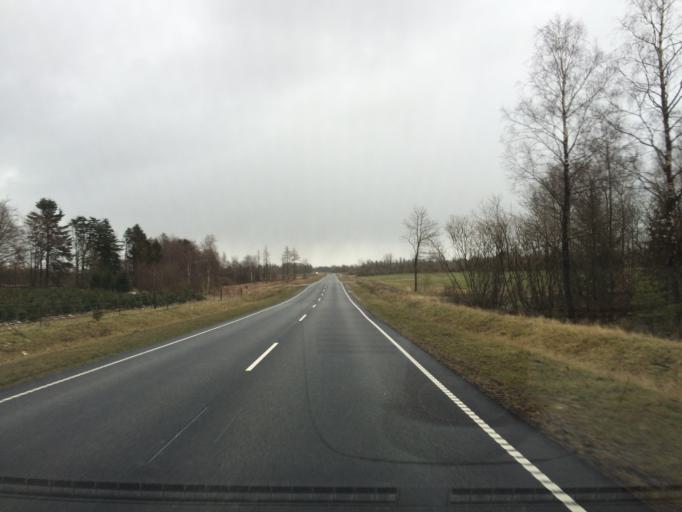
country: DK
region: Central Jutland
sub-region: Herning Kommune
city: Vildbjerg
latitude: 56.1826
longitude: 8.6767
